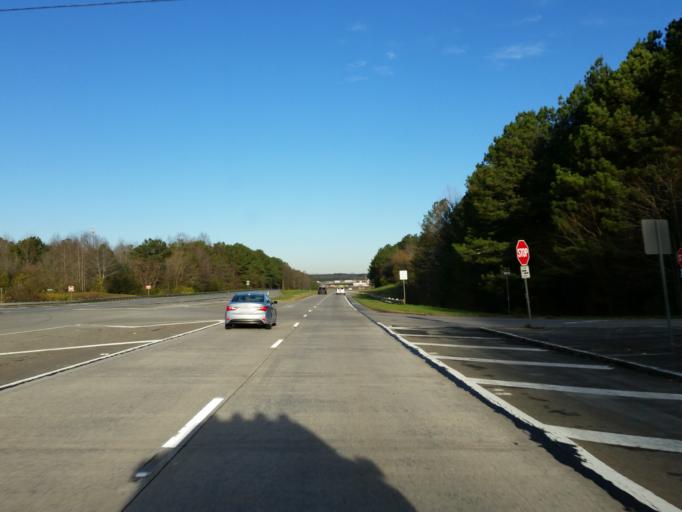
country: US
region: Georgia
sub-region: Pickens County
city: Nelson
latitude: 34.3908
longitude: -84.4055
